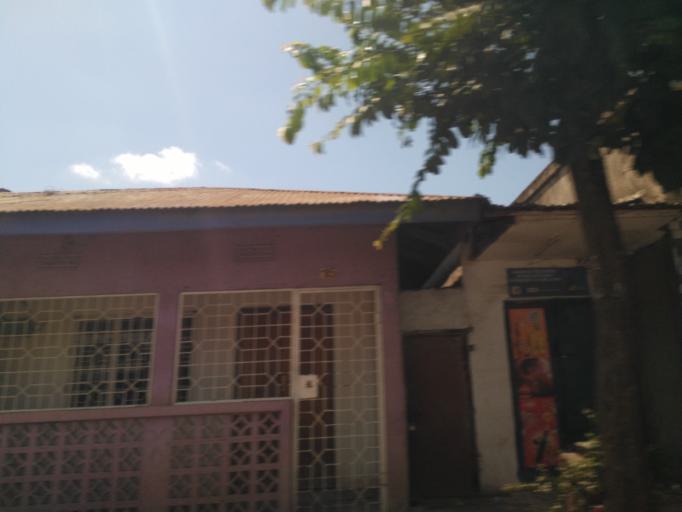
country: TZ
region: Arusha
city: Arusha
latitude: -3.3671
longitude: 36.6863
